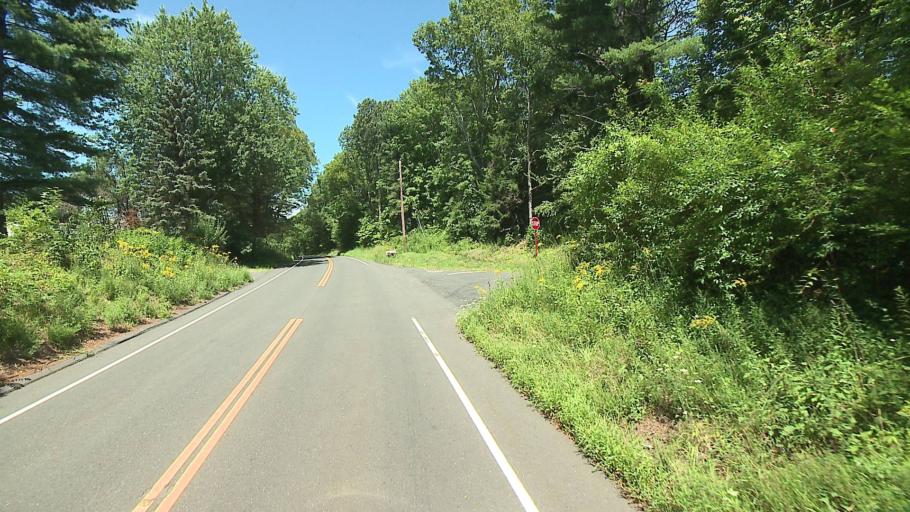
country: US
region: Connecticut
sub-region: Litchfield County
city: New Hartford Center
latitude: 41.9367
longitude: -72.9704
